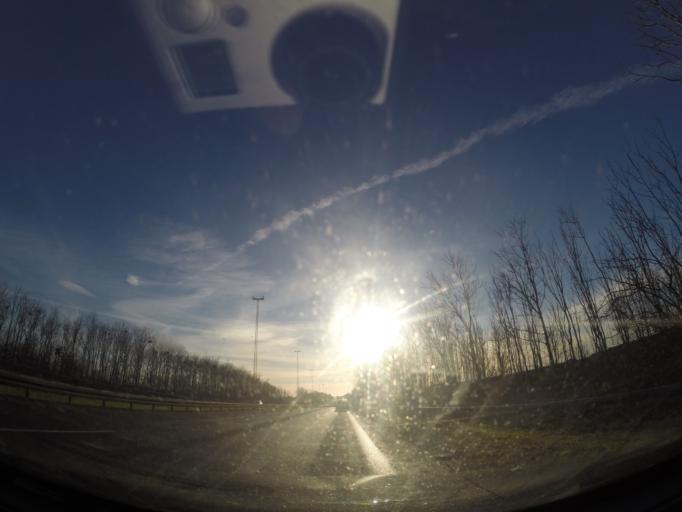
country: DK
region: Capital Region
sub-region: Hoje-Taastrup Kommune
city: Taastrup
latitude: 55.6494
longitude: 12.2819
